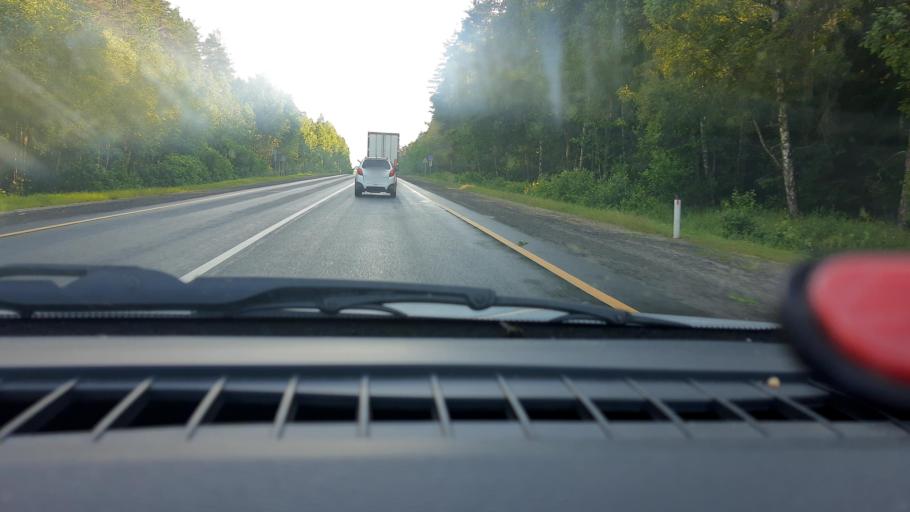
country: RU
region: Nizjnij Novgorod
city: Arzamas
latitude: 55.5100
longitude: 43.8975
